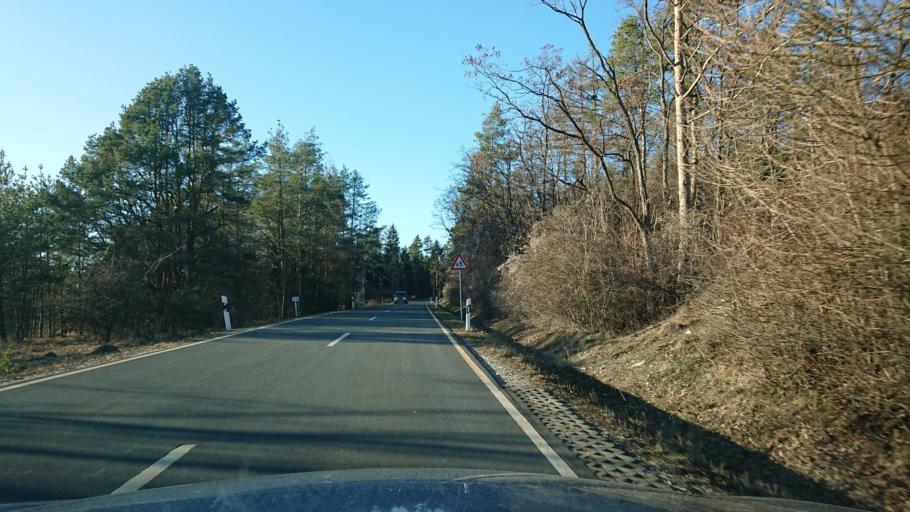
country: DE
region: Bavaria
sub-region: Upper Franconia
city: Ebermannstadt
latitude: 49.7831
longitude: 11.1618
